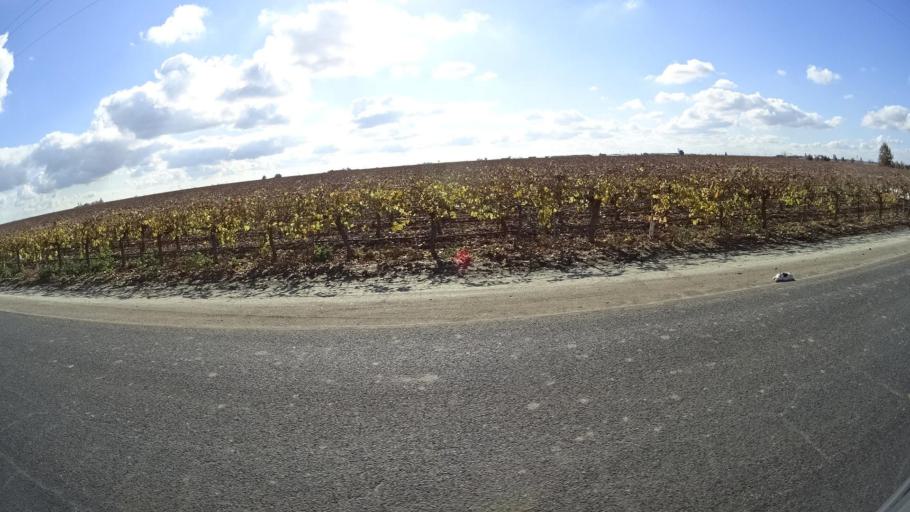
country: US
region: California
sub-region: Kern County
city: McFarland
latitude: 35.6745
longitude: -119.2152
